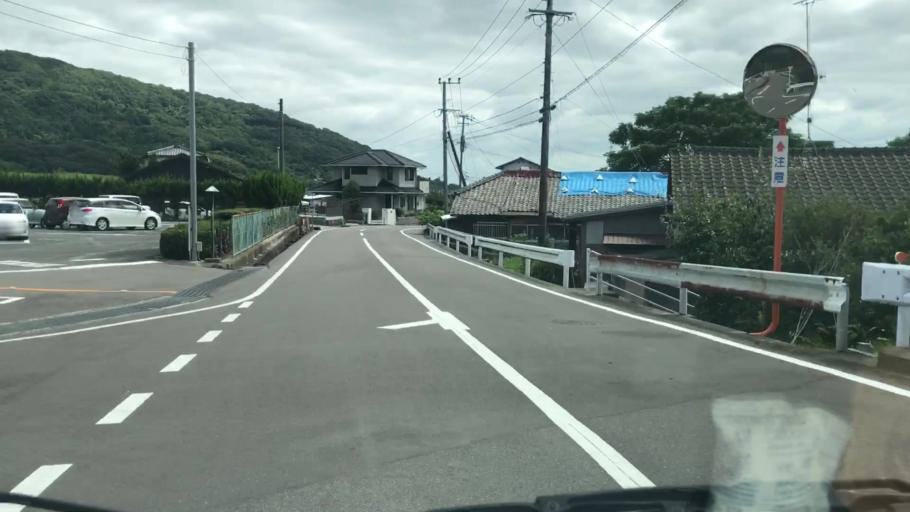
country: JP
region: Saga Prefecture
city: Takeocho-takeo
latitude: 33.2315
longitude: 130.1438
